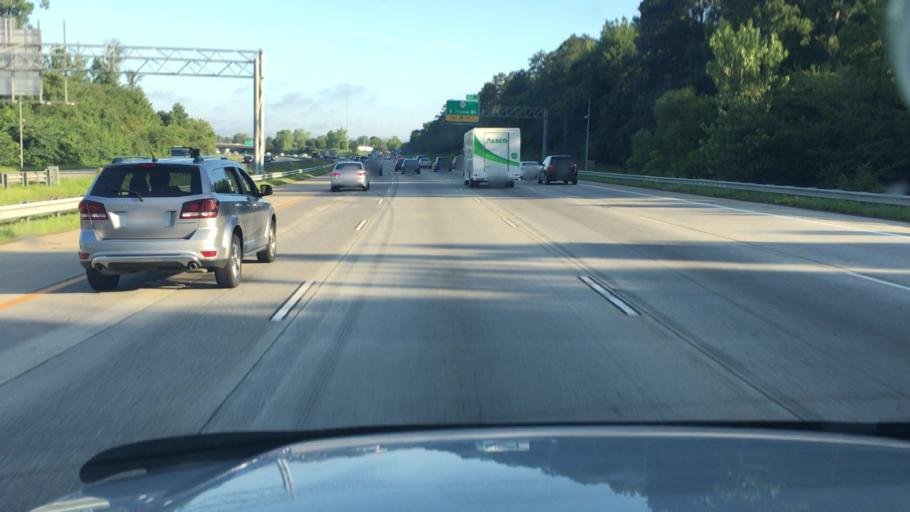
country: US
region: North Carolina
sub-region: Mecklenburg County
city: Pineville
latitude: 35.1366
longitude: -80.9260
